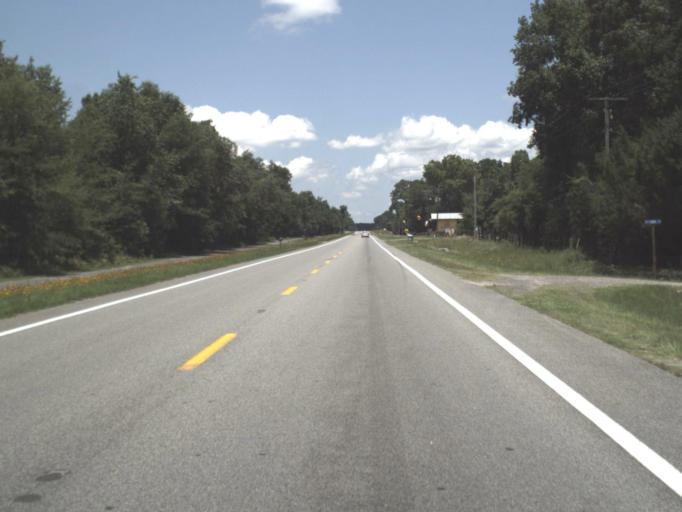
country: US
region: Florida
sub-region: Alachua County
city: High Springs
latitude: 29.9370
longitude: -82.7346
